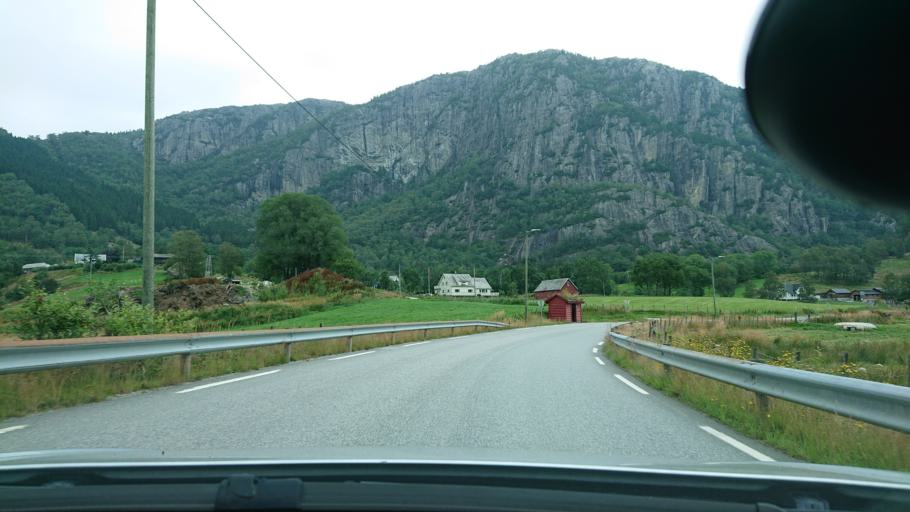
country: NO
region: Rogaland
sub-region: Hjelmeland
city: Hjelmelandsvagen
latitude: 59.2321
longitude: 6.1974
